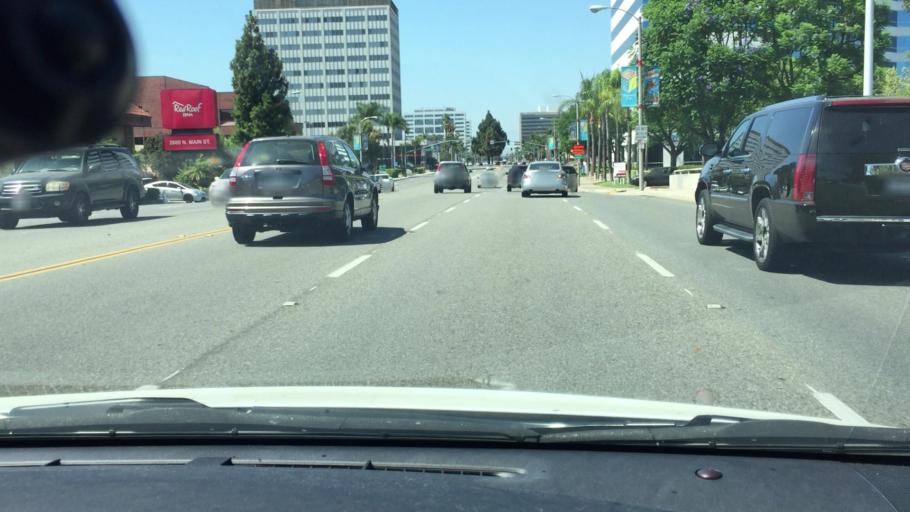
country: US
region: California
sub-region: Orange County
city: Orange
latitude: 33.7710
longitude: -117.8673
